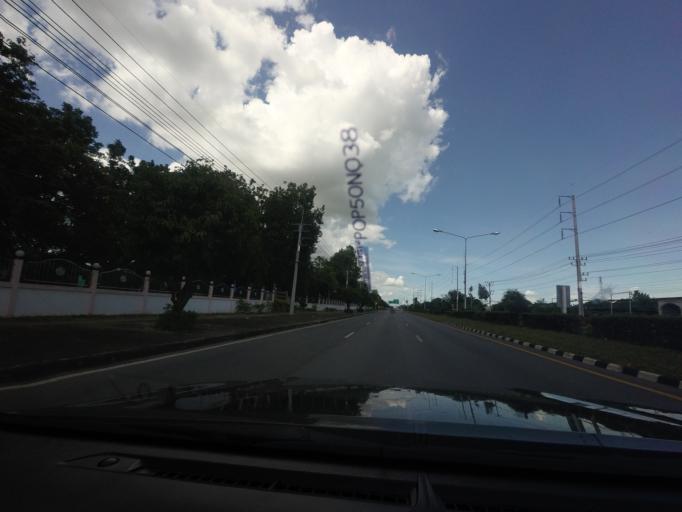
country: TH
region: Kanchanaburi
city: Phanom Thuan
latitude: 14.1250
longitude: 99.6901
